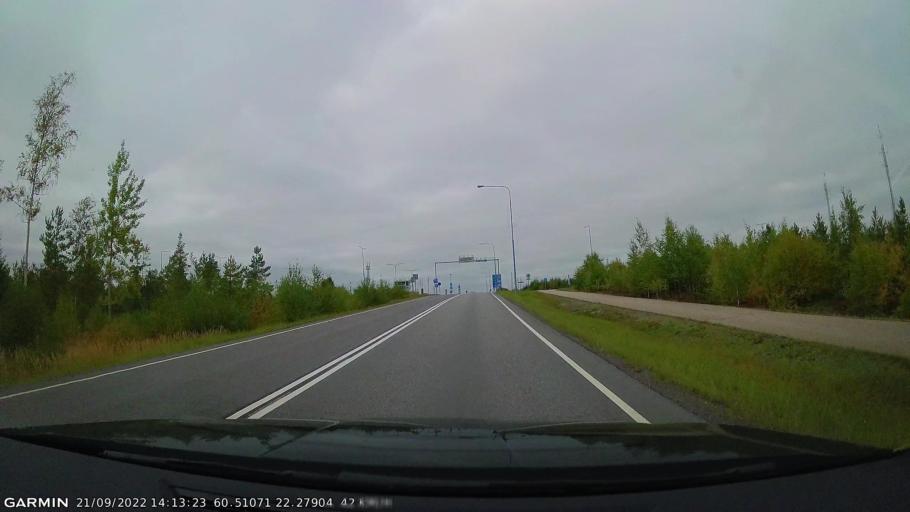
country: FI
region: Varsinais-Suomi
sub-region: Turku
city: Turku
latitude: 60.5107
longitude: 22.2790
